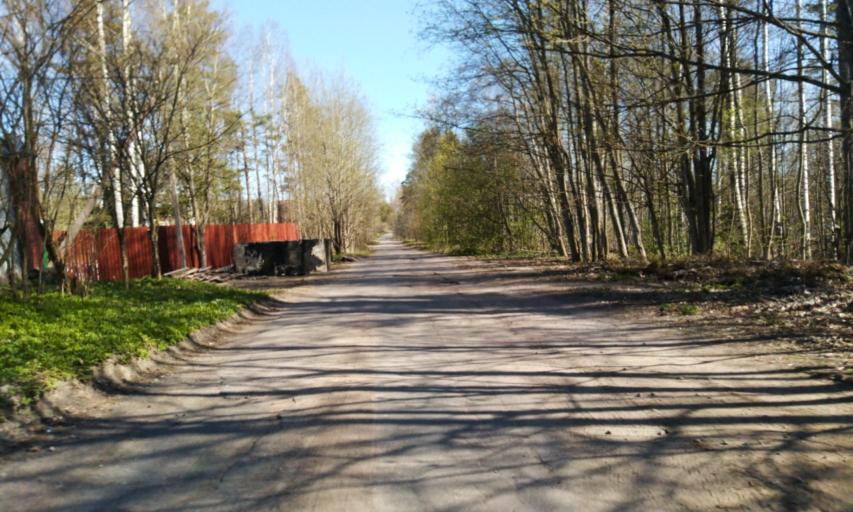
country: RU
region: Leningrad
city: Garbolovo
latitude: 60.3907
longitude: 30.4875
